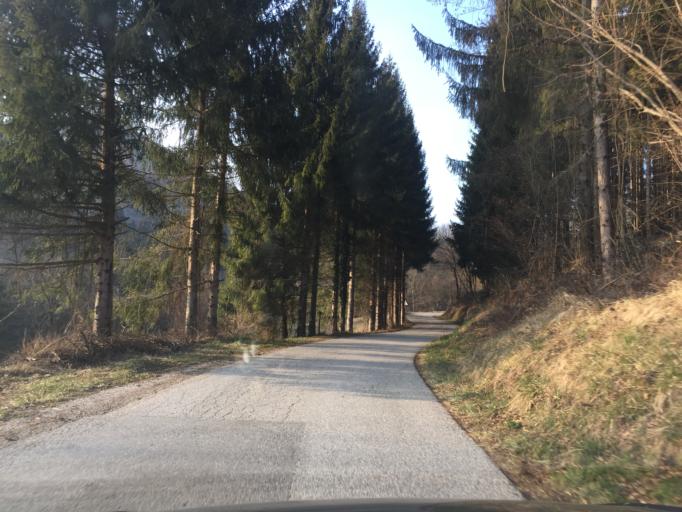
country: SI
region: Kanal
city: Kanal
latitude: 46.0529
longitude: 13.6684
